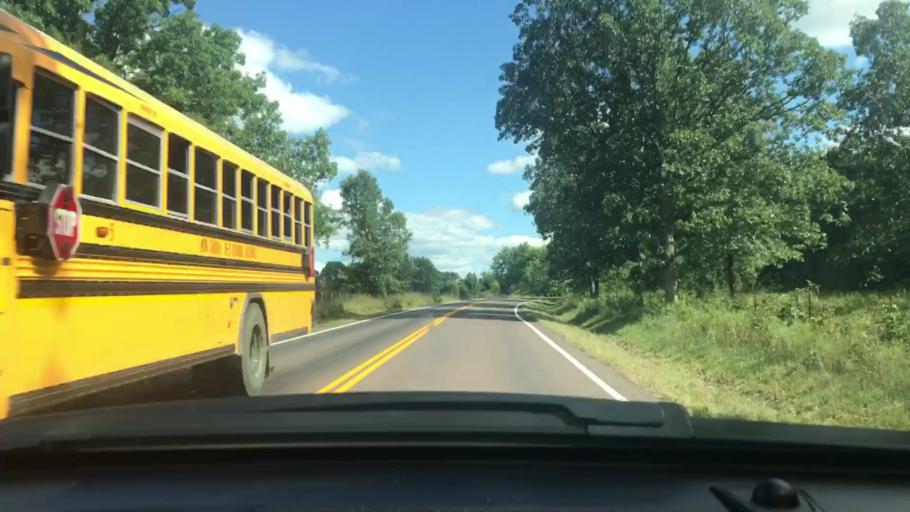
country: US
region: Missouri
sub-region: Wright County
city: Mountain Grove
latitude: 37.2313
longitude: -92.2956
